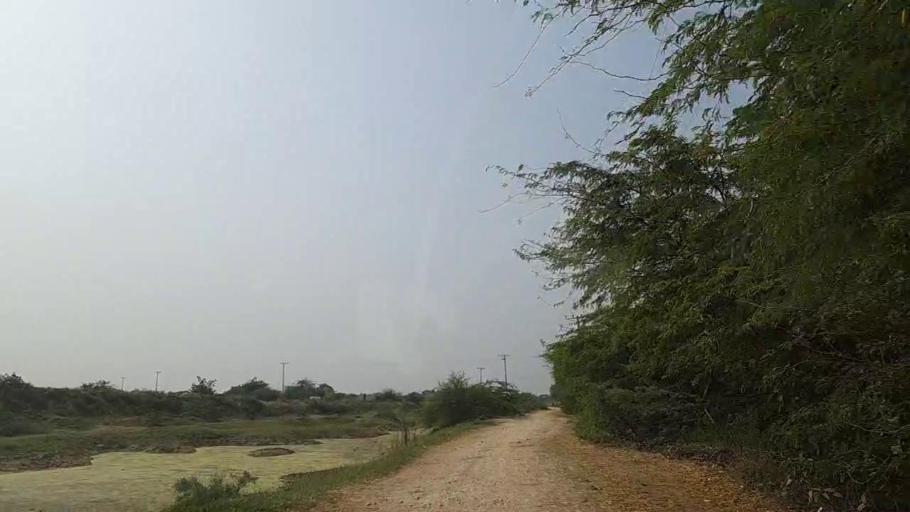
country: PK
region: Sindh
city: Mirpur Sakro
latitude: 24.6160
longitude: 67.7334
